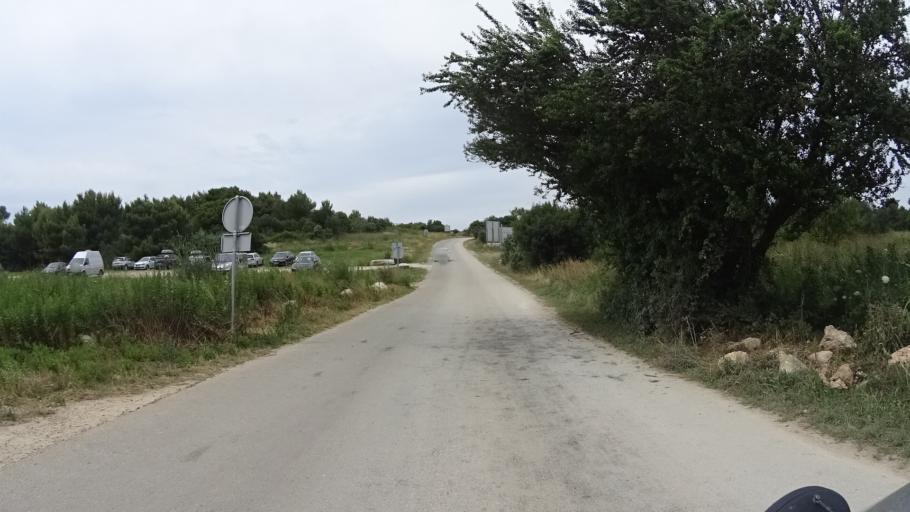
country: HR
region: Istarska
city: Medulin
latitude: 44.7979
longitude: 13.9064
